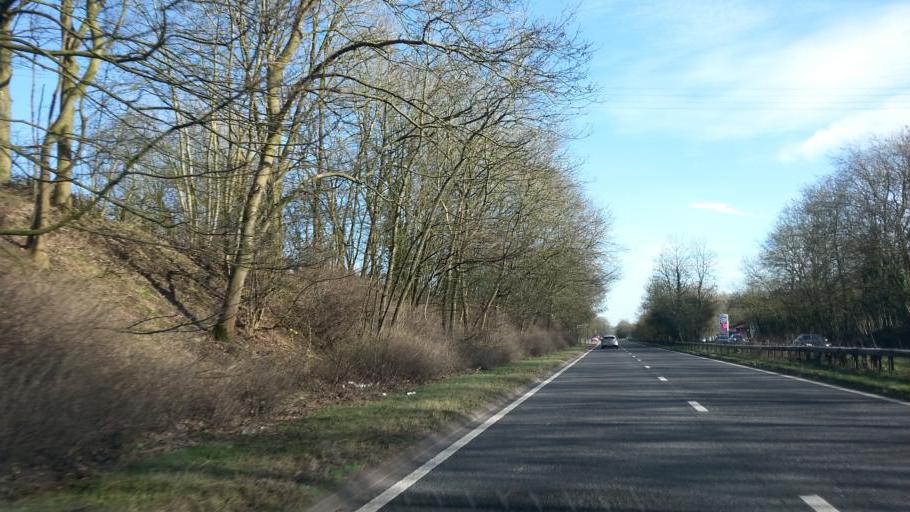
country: GB
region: England
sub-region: Solihull
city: Meriden
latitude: 52.4361
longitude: -1.6067
